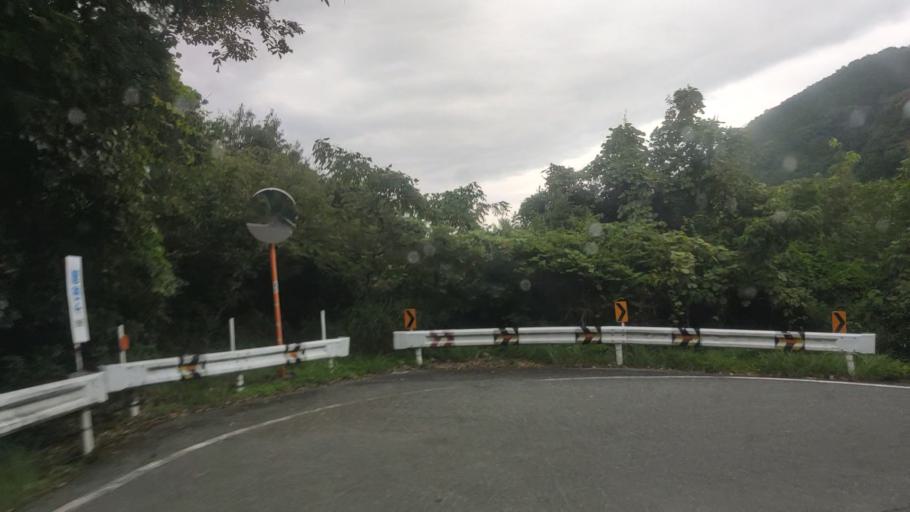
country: JP
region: Wakayama
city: Hashimoto
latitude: 34.2970
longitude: 135.6299
